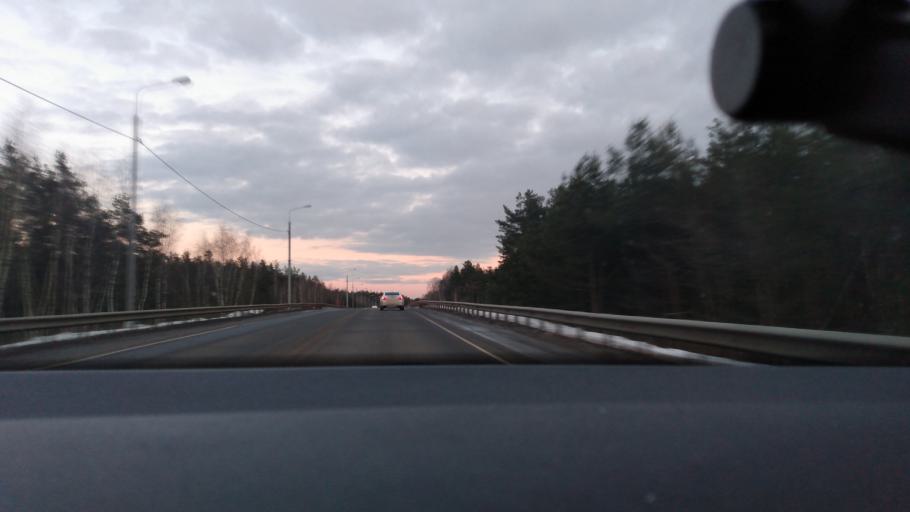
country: RU
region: Moskovskaya
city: Il'inskiy Pogost
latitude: 55.4874
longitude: 38.9067
